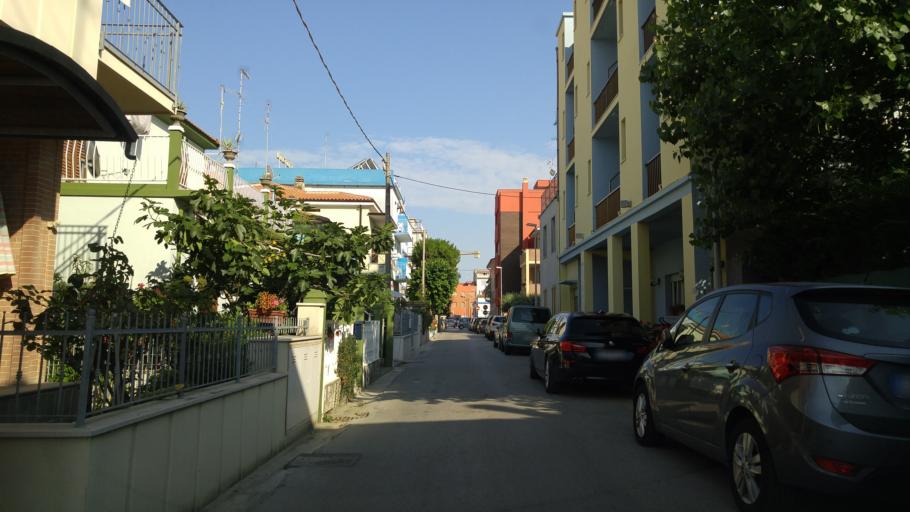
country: IT
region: The Marches
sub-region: Provincia di Pesaro e Urbino
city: Marotta
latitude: 43.7743
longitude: 13.1305
